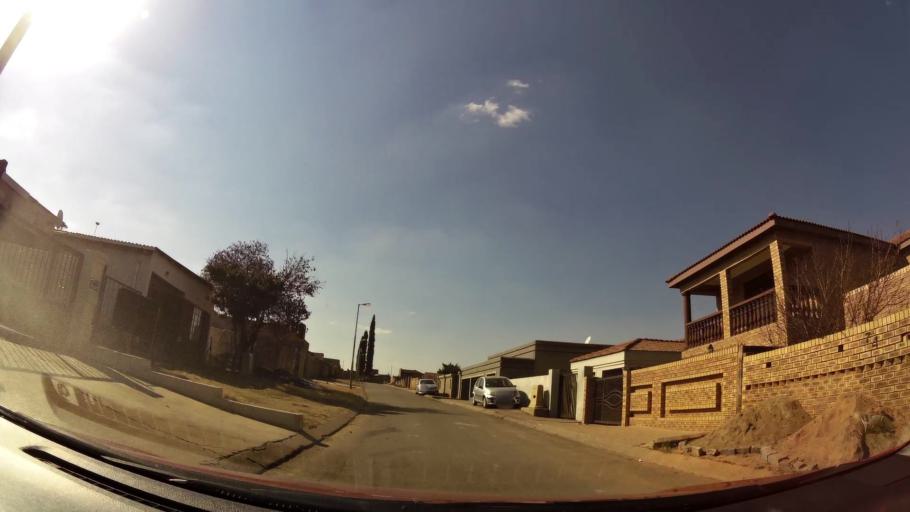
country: ZA
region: Gauteng
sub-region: City of Johannesburg Metropolitan Municipality
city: Soweto
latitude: -26.2355
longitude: 27.8801
